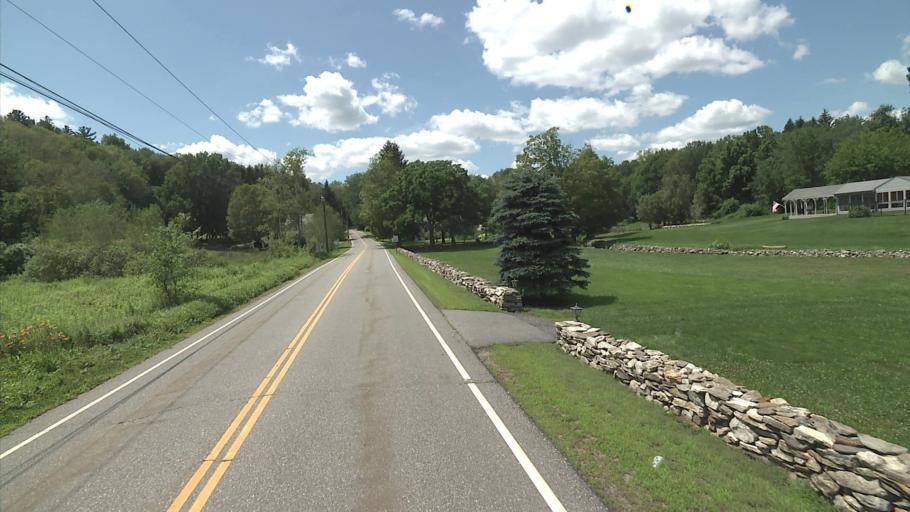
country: US
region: Connecticut
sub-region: Windham County
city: Quinebaug
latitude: 41.9922
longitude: -71.9998
